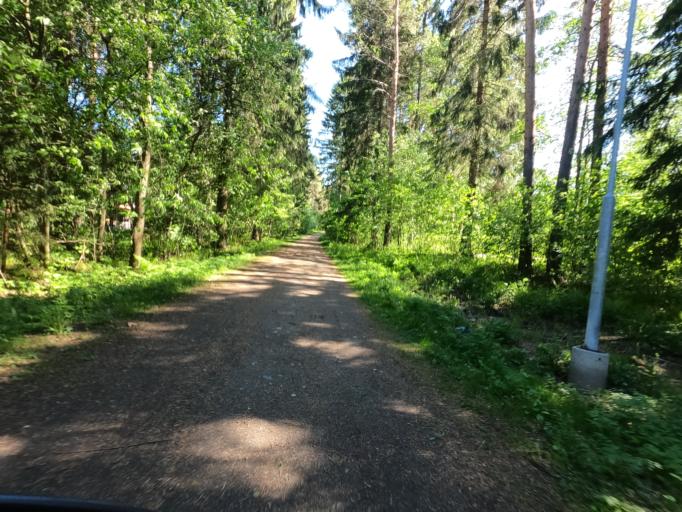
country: FI
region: North Karelia
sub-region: Joensuu
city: Joensuu
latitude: 62.5906
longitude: 29.7991
